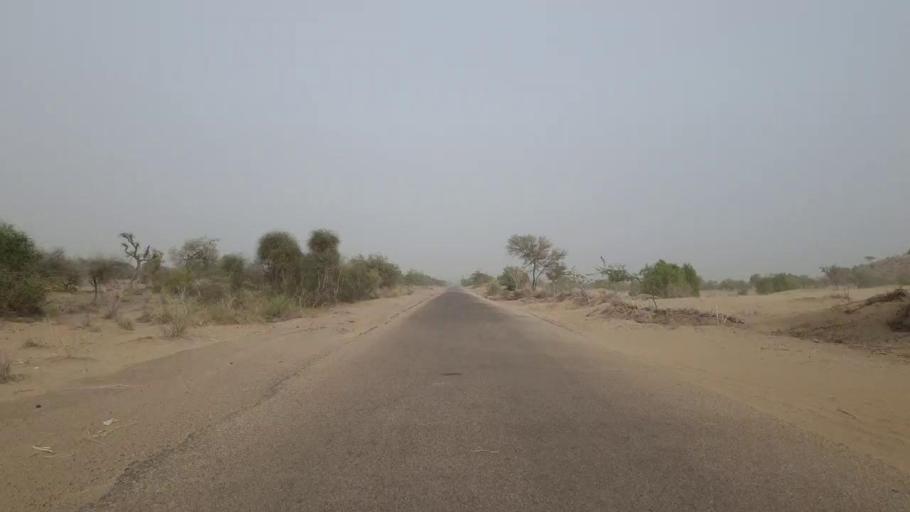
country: PK
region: Sindh
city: Islamkot
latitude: 24.5784
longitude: 70.3076
